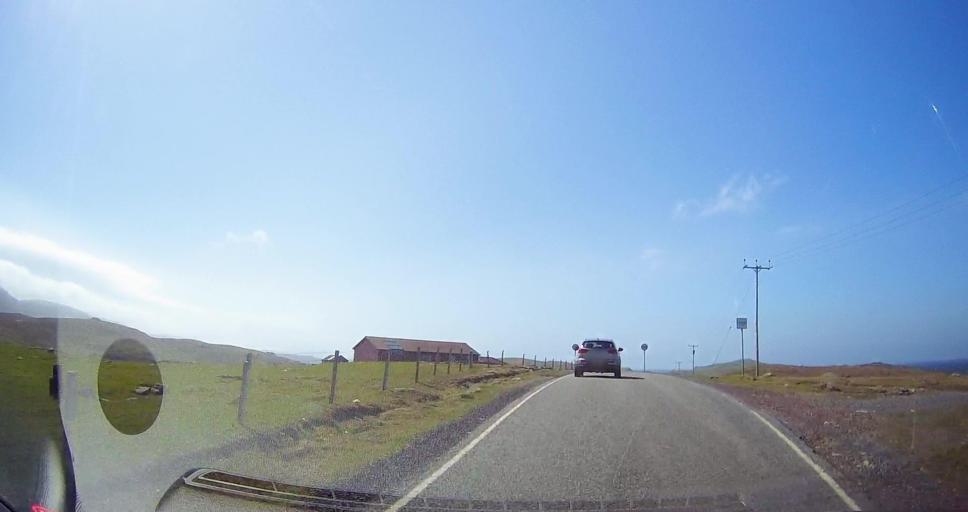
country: GB
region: Scotland
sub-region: Shetland Islands
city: Sandwick
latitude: 60.0901
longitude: -1.3259
